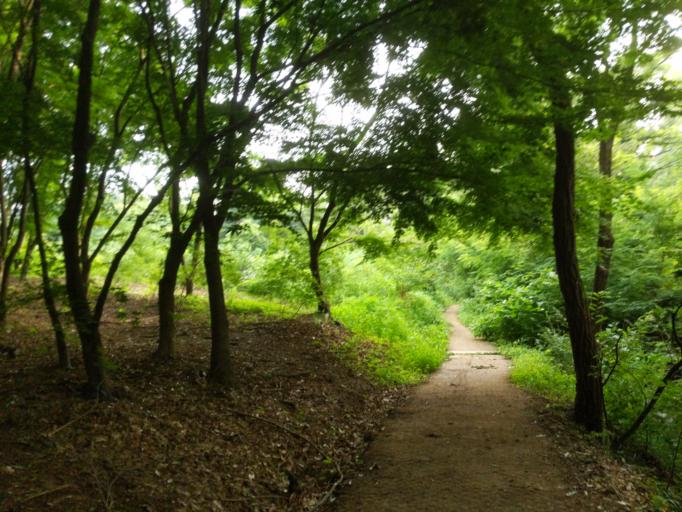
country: KR
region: Daegu
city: Hwawon
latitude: 35.8006
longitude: 128.5270
